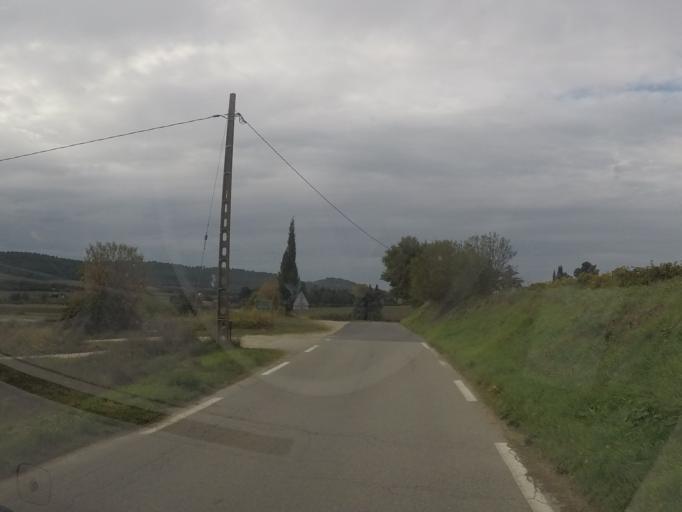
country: FR
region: Provence-Alpes-Cote d'Azur
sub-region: Departement du Vaucluse
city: Ansouis
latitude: 43.7436
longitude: 5.4433
